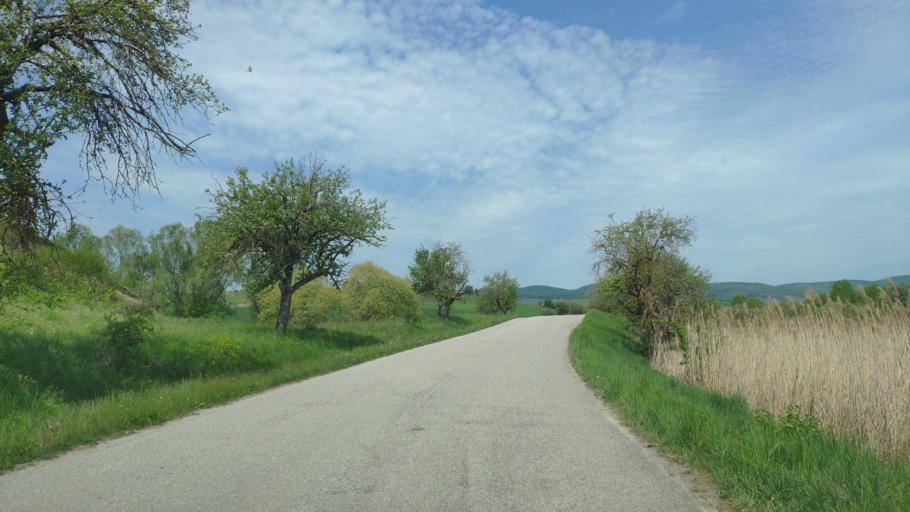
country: SK
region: Banskobystricky
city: Rimavska Sobota
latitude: 48.4249
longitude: 20.2156
